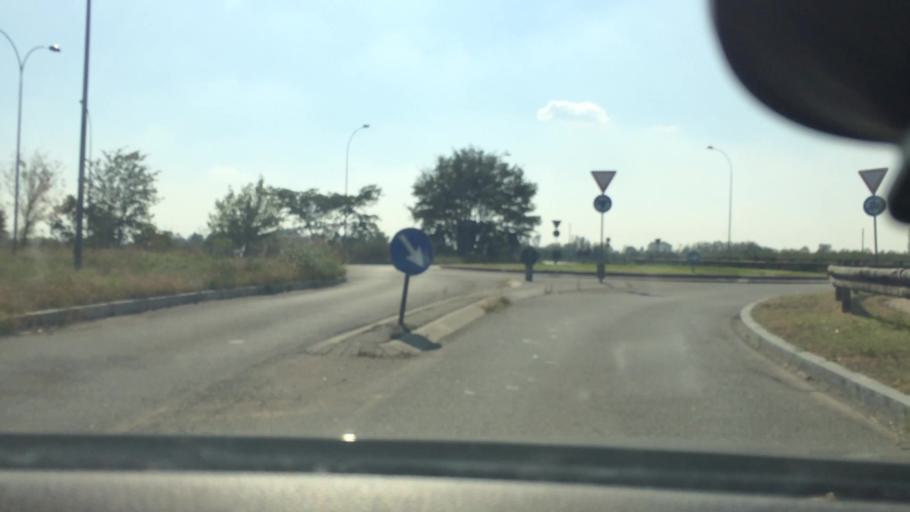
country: IT
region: Lombardy
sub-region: Citta metropolitana di Milano
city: Mesero
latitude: 45.4978
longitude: 8.8464
